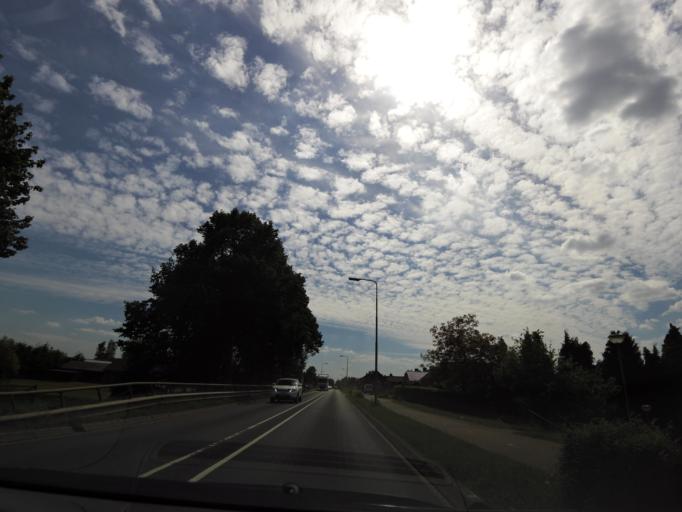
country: NL
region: Limburg
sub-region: Gemeente Leudal
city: Haelen
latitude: 51.2613
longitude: 5.9846
